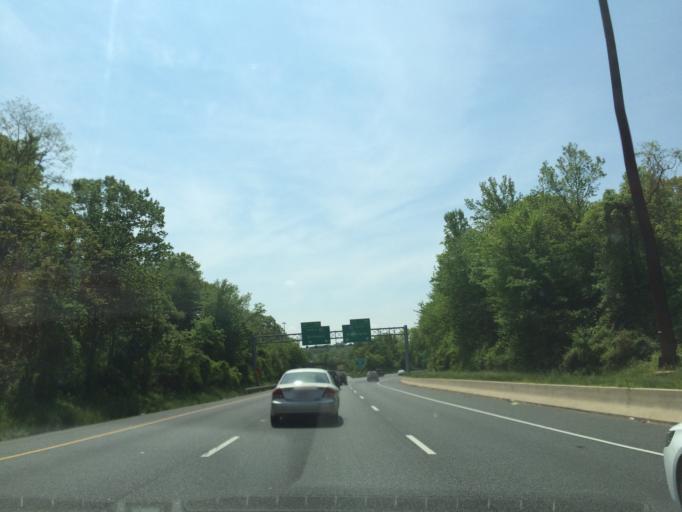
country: US
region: Maryland
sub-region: Baltimore County
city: Arbutus
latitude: 39.2526
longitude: -76.6839
